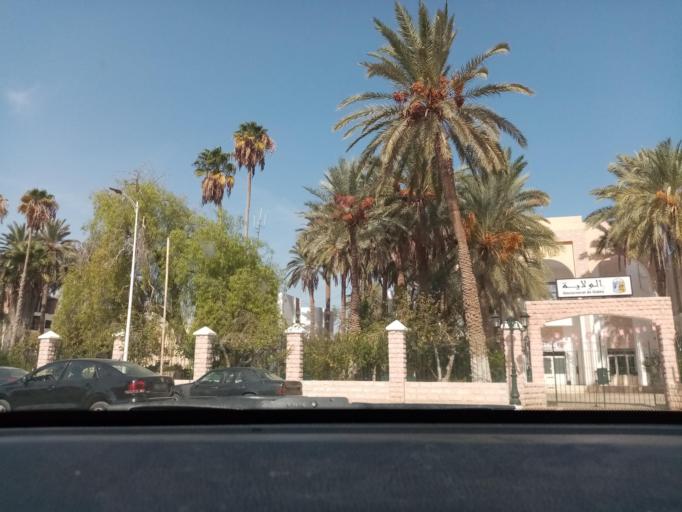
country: TN
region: Qabis
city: Gabes
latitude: 33.8870
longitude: 10.1002
